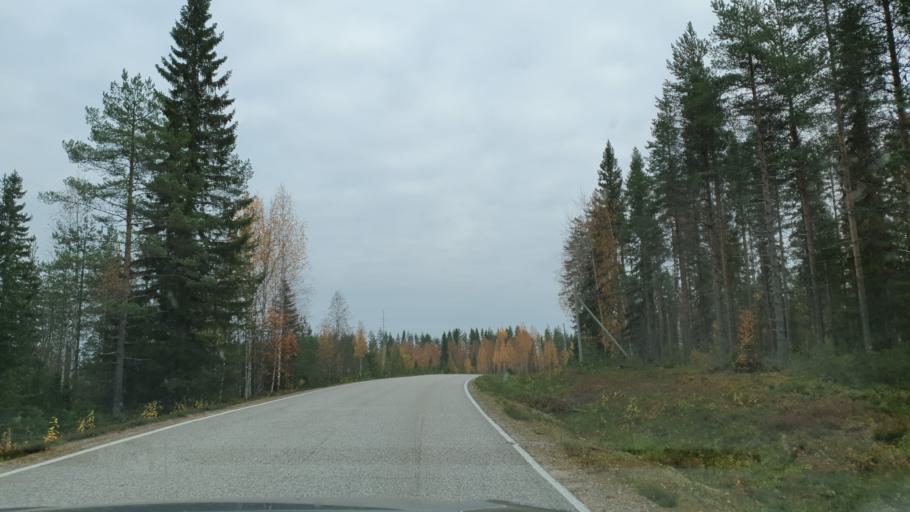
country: FI
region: Kainuu
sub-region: Kajaani
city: Ristijaervi
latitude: 64.4506
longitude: 28.3591
